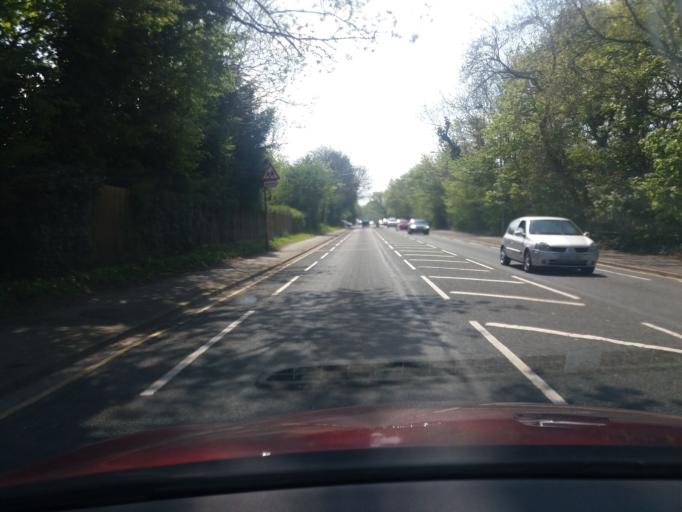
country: GB
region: England
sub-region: Lancashire
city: Clayton-le-Woods
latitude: 53.6910
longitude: -2.6389
